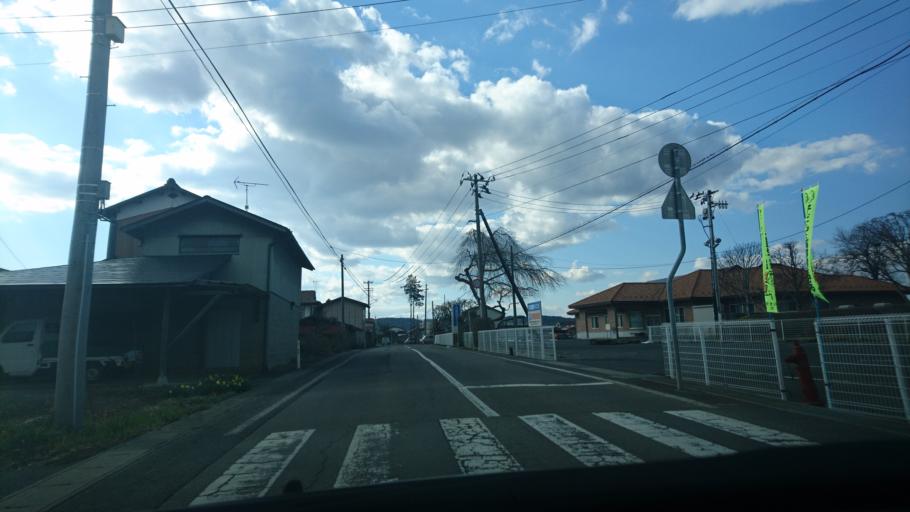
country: JP
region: Iwate
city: Mizusawa
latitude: 39.0429
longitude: 141.1401
